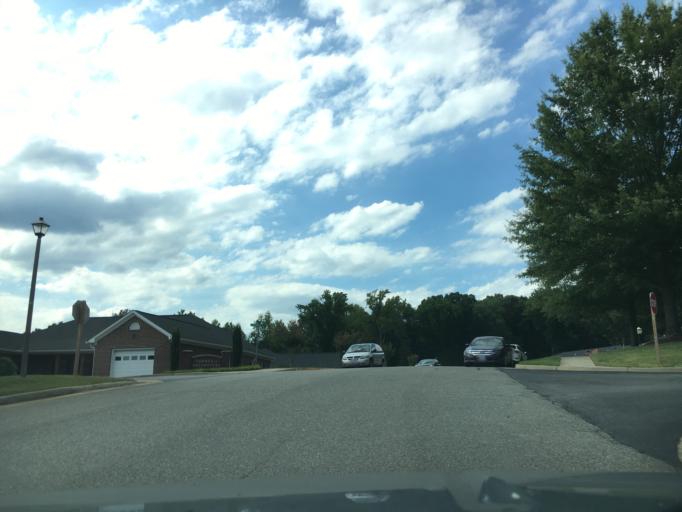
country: US
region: Virginia
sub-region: Halifax County
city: South Boston
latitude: 36.7140
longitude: -78.9172
